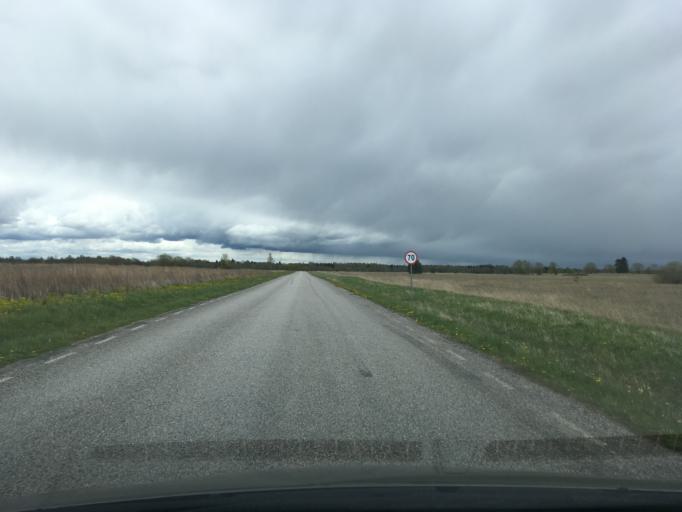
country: EE
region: Harju
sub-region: Rae vald
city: Vaida
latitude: 59.3577
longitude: 24.9779
